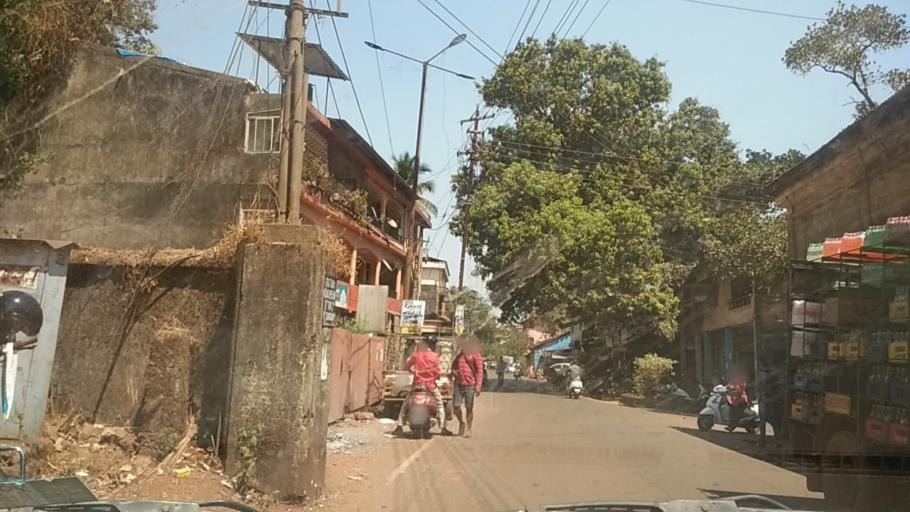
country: IN
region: Goa
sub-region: North Goa
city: Dicholi
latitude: 15.5879
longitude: 73.9443
